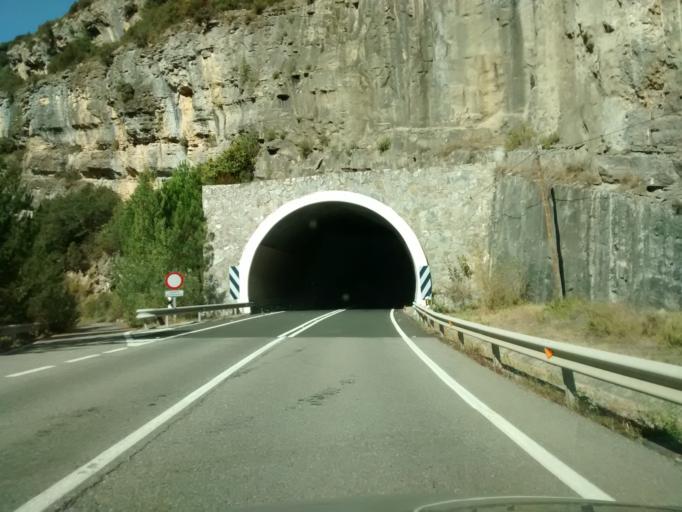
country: ES
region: Aragon
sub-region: Provincia de Huesca
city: Boltana
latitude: 42.4636
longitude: 0.0363
